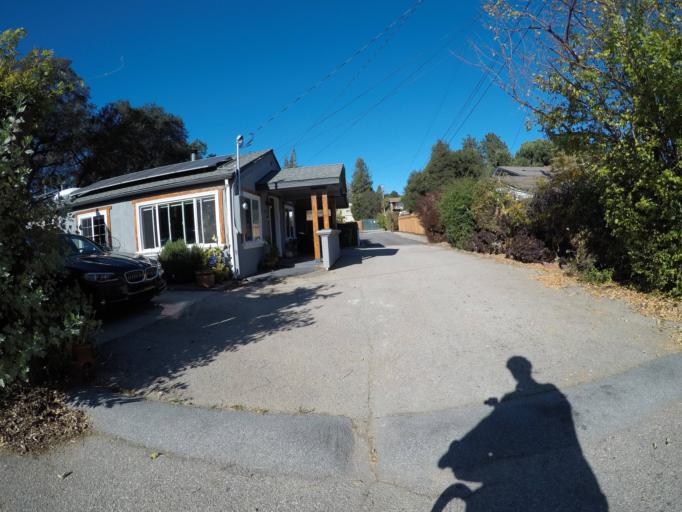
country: US
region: California
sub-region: Santa Cruz County
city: Scotts Valley
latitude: 37.0464
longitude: -122.0221
